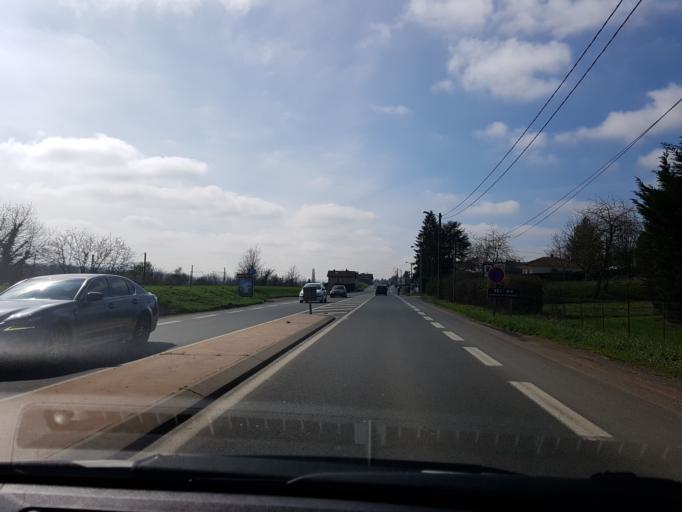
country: FR
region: Rhone-Alpes
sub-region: Departement du Rhone
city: Villefranche-sur-Saone
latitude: 45.9641
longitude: 4.7160
